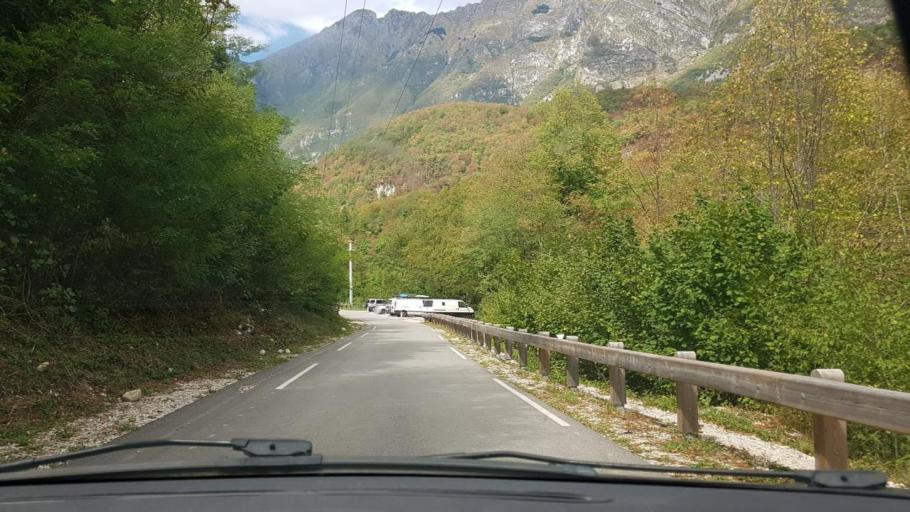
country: SI
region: Kobarid
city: Kobarid
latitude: 46.2566
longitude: 13.5862
